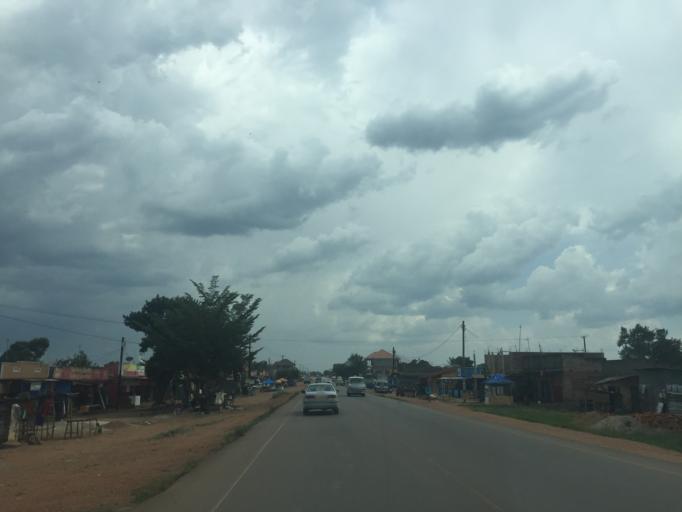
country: UG
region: Central Region
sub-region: Luwero District
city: Wobulenzi
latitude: 0.6843
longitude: 32.5234
